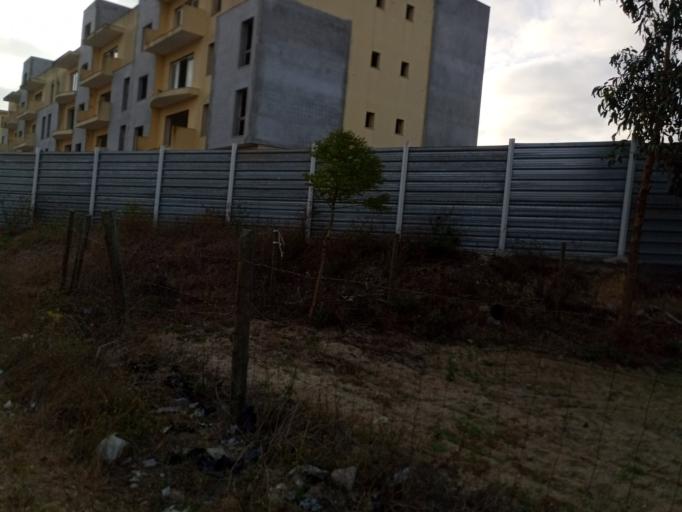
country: PT
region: Leiria
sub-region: Caldas da Rainha
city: Caldas da Rainha
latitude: 39.4157
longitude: -9.1458
